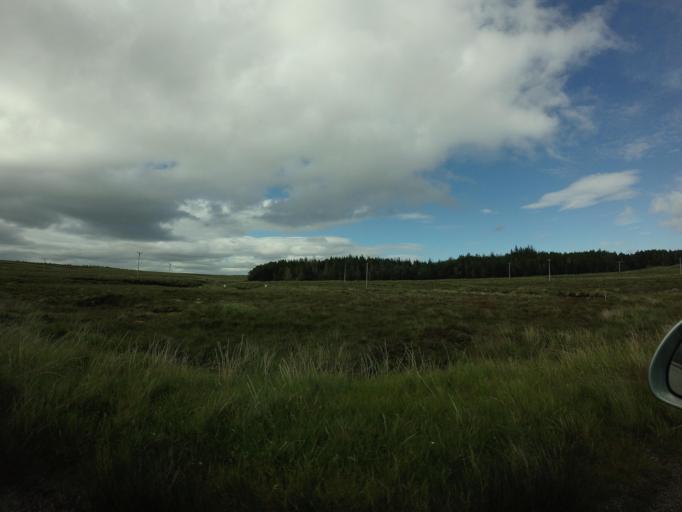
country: GB
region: Scotland
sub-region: Eilean Siar
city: Isle of Lewis
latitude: 58.1822
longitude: -6.6656
